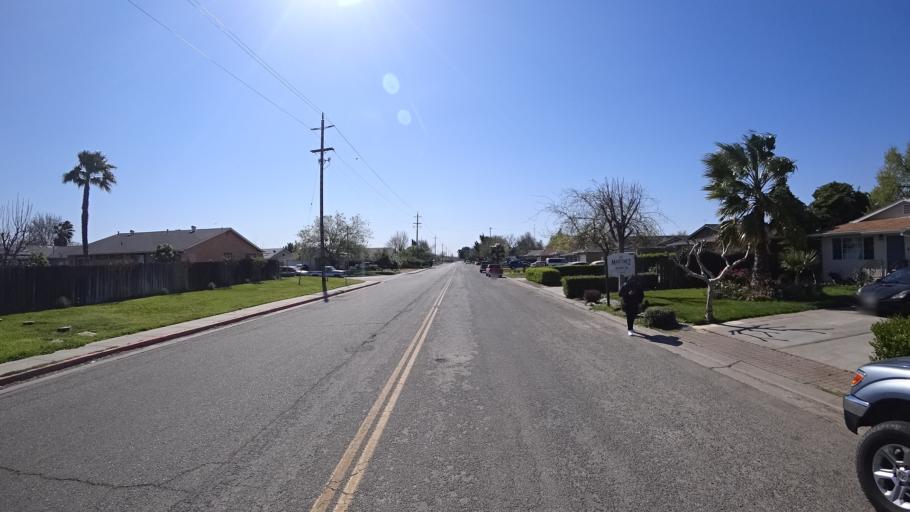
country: US
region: California
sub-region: Glenn County
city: Hamilton City
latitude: 39.7456
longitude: -122.0084
